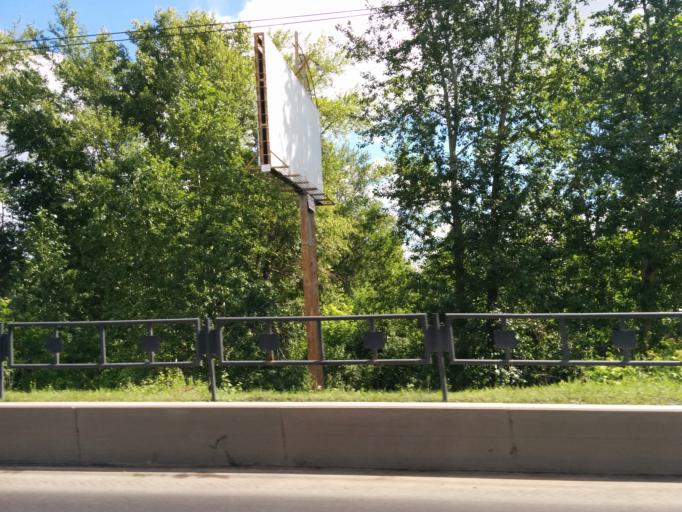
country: RU
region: Perm
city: Perm
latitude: 58.0257
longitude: 56.2188
